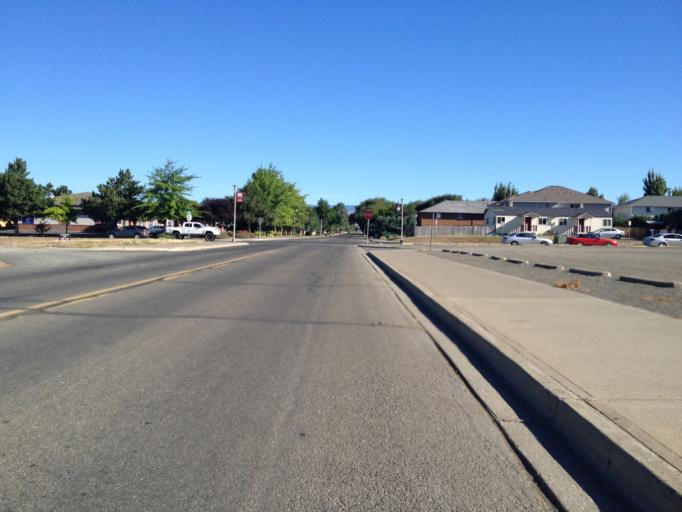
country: US
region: Washington
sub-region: Kittitas County
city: Ellensburg
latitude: 47.0098
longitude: -120.5396
